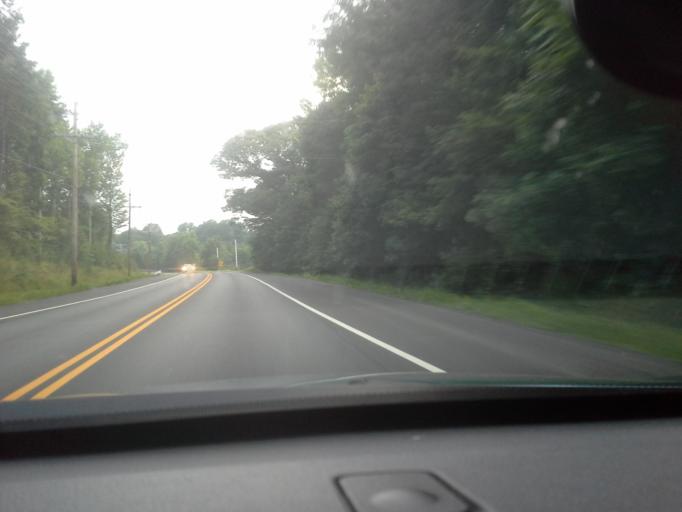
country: US
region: Maryland
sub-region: Calvert County
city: Prince Frederick
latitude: 38.5569
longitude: -76.5504
